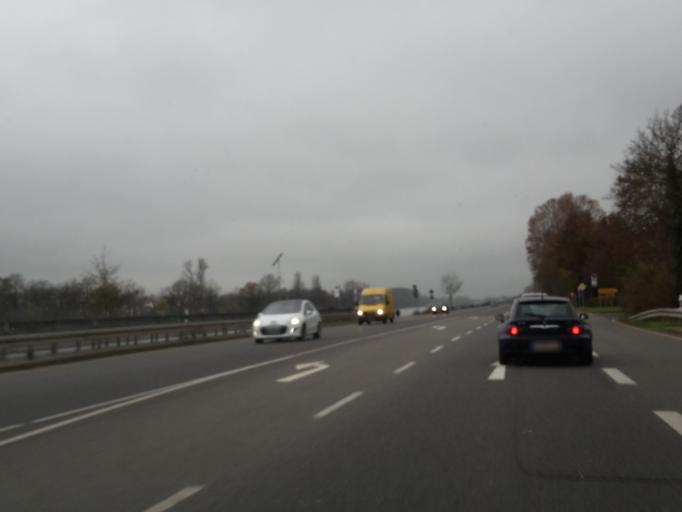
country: DE
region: Hesse
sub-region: Regierungsbezirk Darmstadt
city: Kiedrich
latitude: 50.0191
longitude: 8.0978
